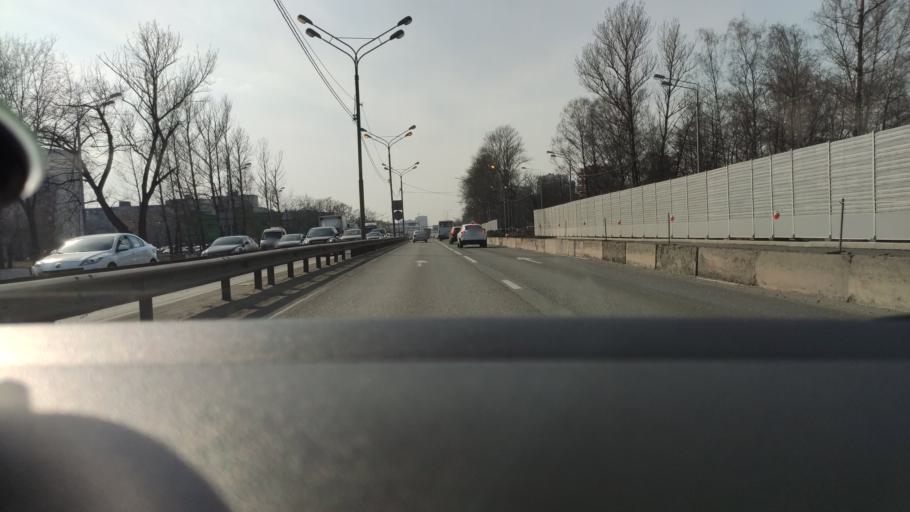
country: RU
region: Moskovskaya
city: Balashikha
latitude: 55.7984
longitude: 37.9762
